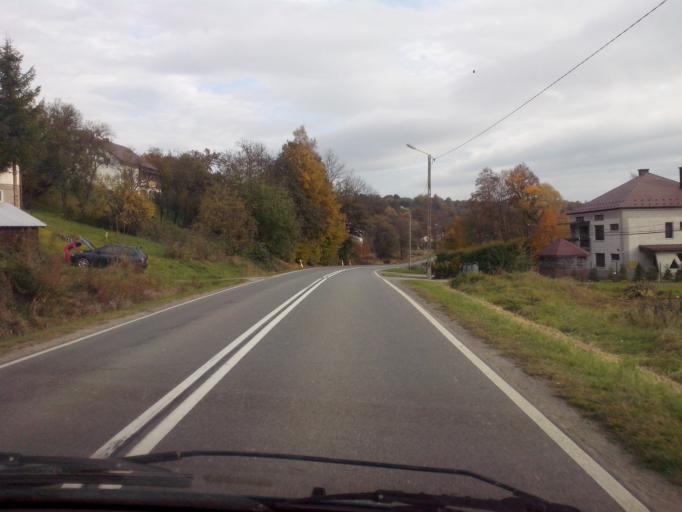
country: PL
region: Subcarpathian Voivodeship
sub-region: Powiat strzyzowski
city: Wisniowa
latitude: 49.8998
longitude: 21.6376
